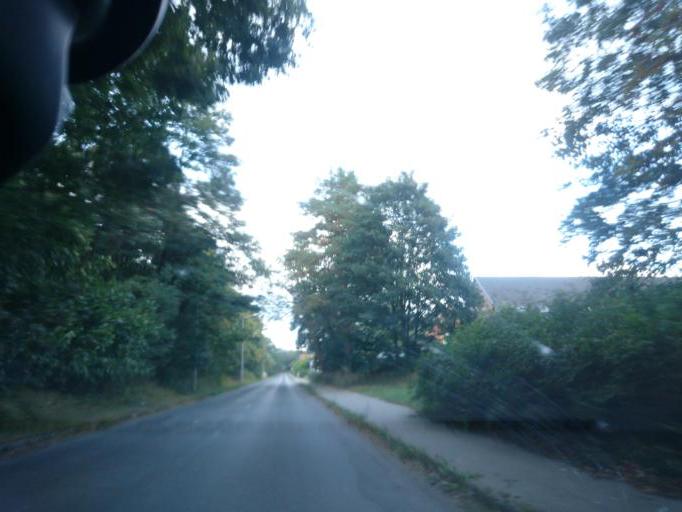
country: DE
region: Mecklenburg-Vorpommern
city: Kritzmow
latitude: 54.0757
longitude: 12.0795
